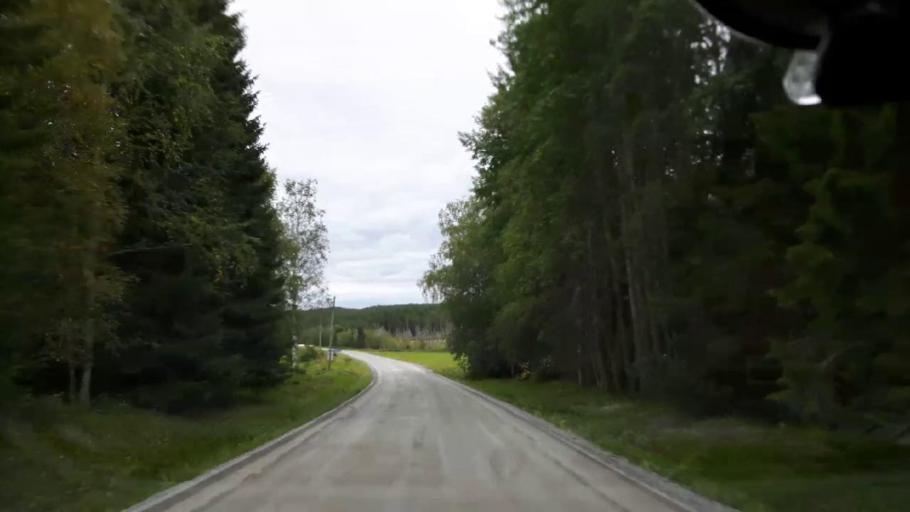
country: SE
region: Jaemtland
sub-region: OEstersunds Kommun
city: Brunflo
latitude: 63.0892
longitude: 15.1450
